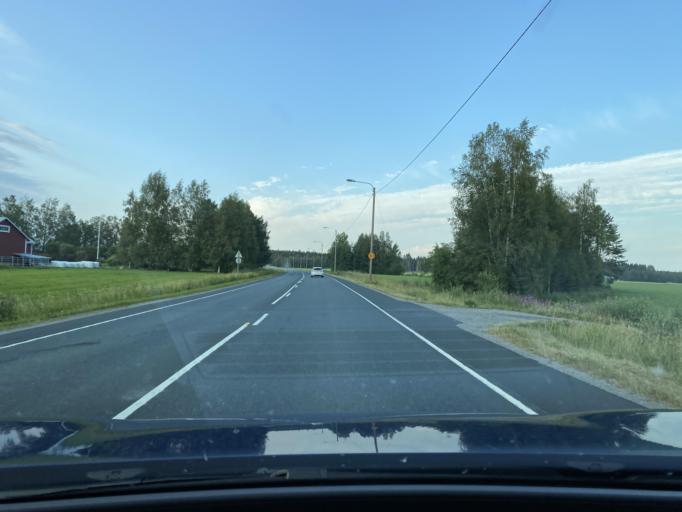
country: FI
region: Ostrobothnia
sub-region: Jakobstadsregionen
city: Bennaes
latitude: 63.6376
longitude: 22.8734
